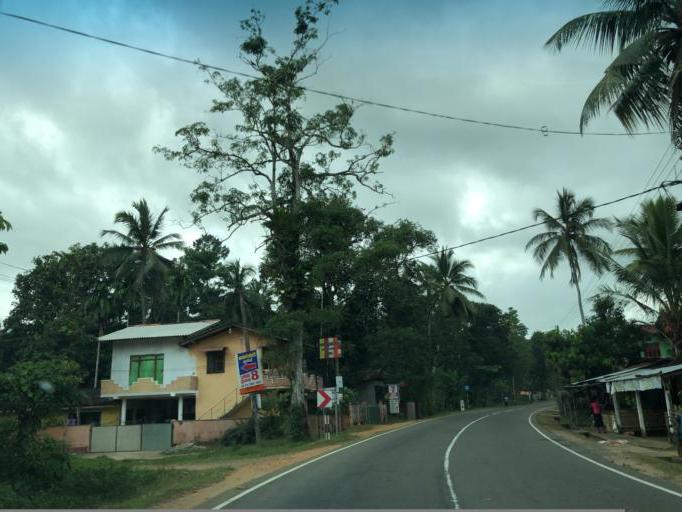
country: LK
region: Western
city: Horana South
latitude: 6.6815
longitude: 80.0952
